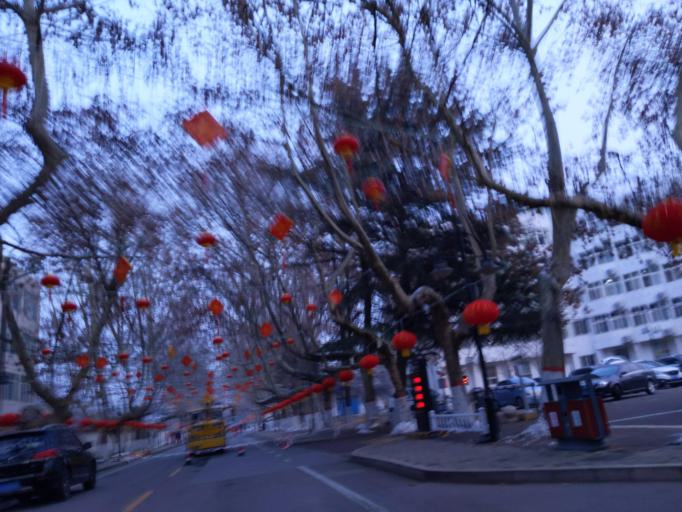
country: CN
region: Henan Sheng
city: Zhongyuanlu
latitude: 35.7777
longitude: 115.0745
